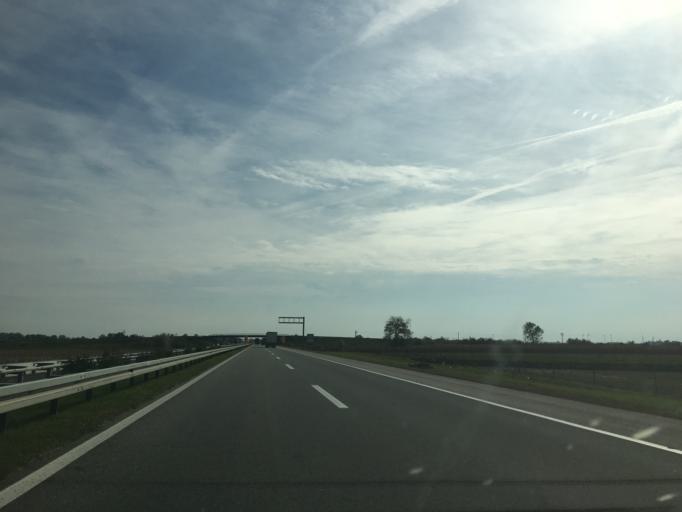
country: RS
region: Autonomna Pokrajina Vojvodina
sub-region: Sremski Okrug
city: Stara Pazova
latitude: 45.0144
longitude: 20.1968
